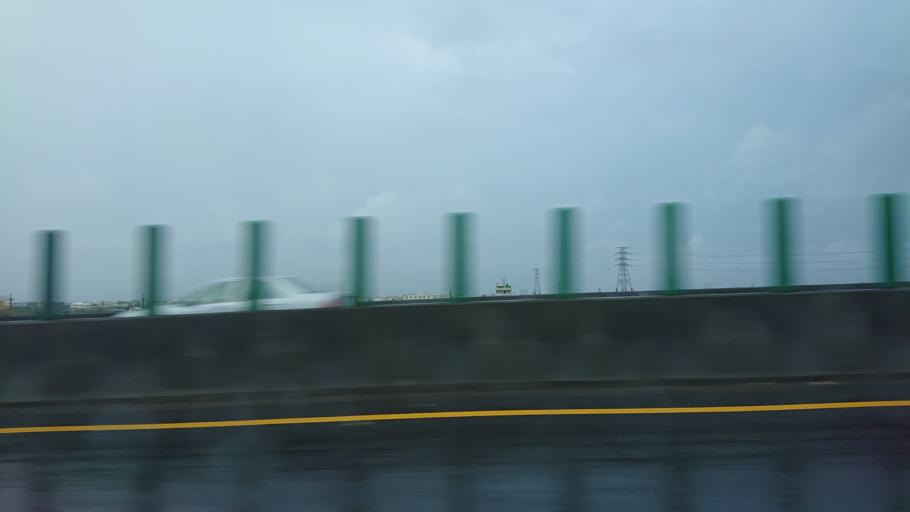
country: TW
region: Taiwan
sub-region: Changhua
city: Chang-hua
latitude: 24.1275
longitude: 120.4390
